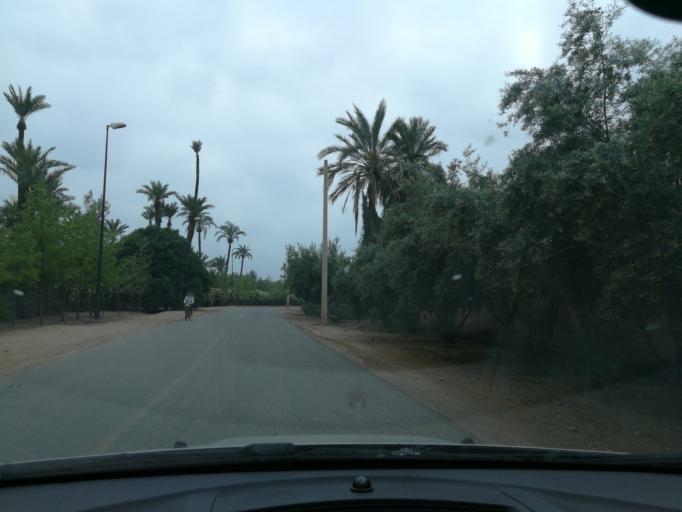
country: MA
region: Marrakech-Tensift-Al Haouz
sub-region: Marrakech
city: Marrakesh
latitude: 31.6699
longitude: -7.9845
